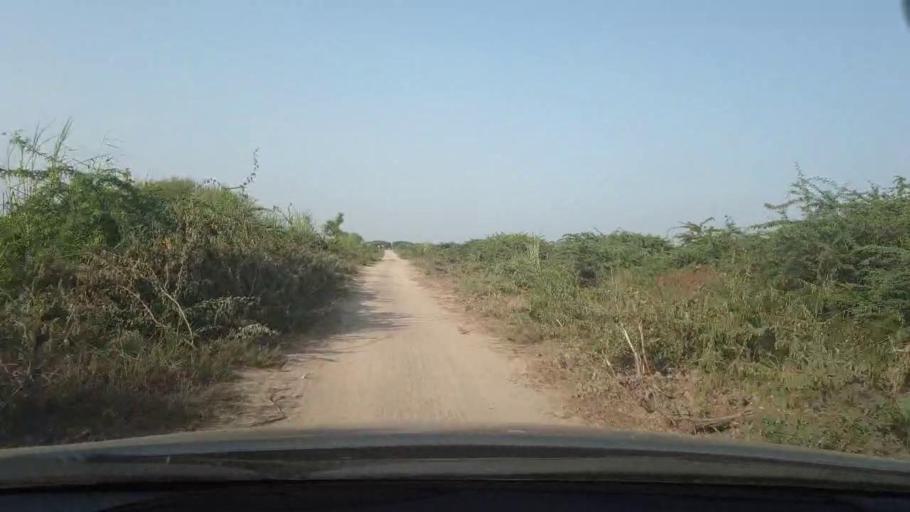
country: PK
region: Sindh
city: Naukot
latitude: 24.7748
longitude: 69.2321
